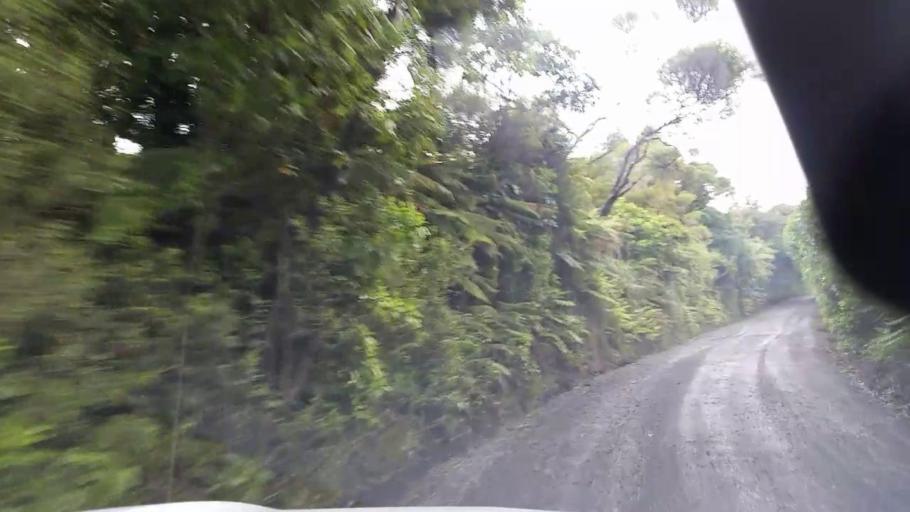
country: NZ
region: Auckland
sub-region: Auckland
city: Titirangi
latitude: -36.9437
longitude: 174.5251
